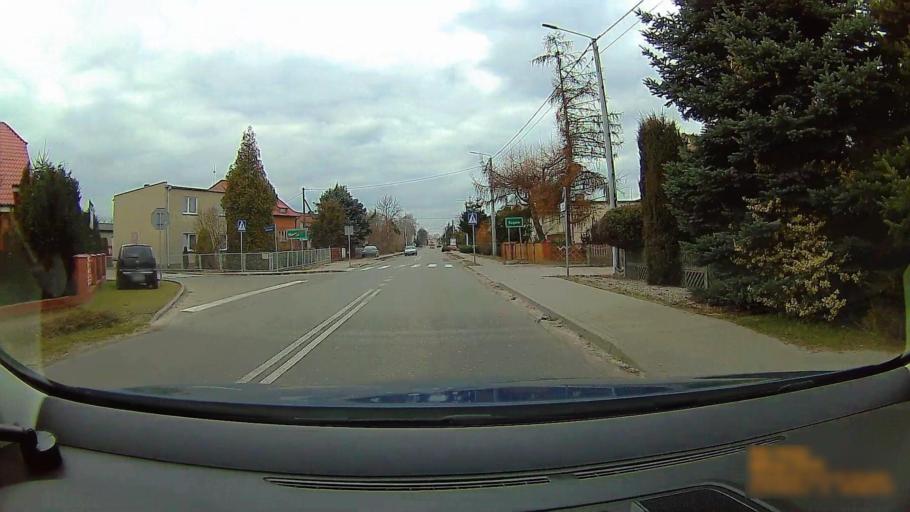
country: PL
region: Greater Poland Voivodeship
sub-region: Powiat koninski
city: Rzgow Pierwszy
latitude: 52.1567
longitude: 18.0559
